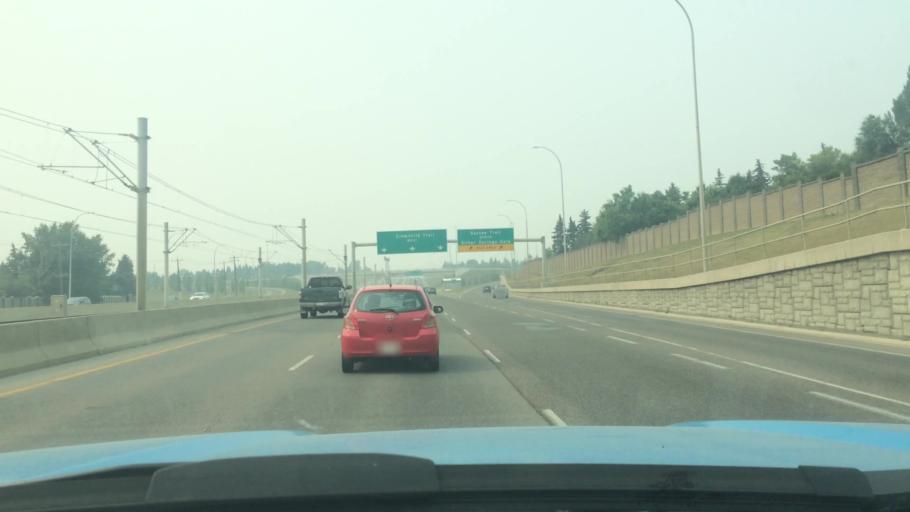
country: CA
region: Alberta
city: Calgary
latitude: 51.1083
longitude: -114.1723
